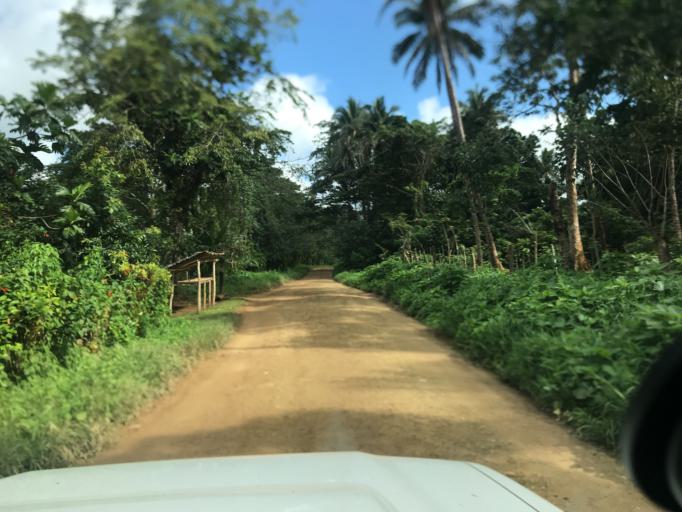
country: VU
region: Sanma
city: Luganville
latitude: -15.4745
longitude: 167.0846
